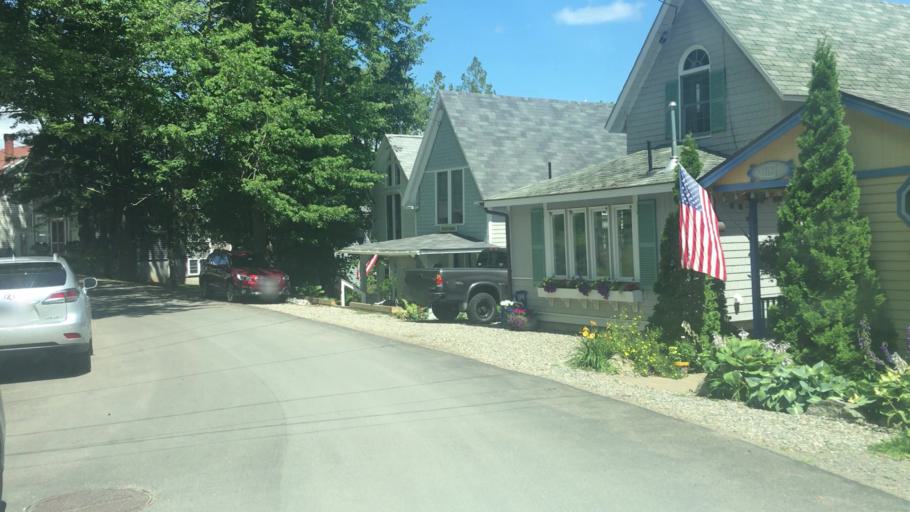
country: US
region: Maine
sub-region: Waldo County
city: Northport
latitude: 44.3795
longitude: -68.9673
